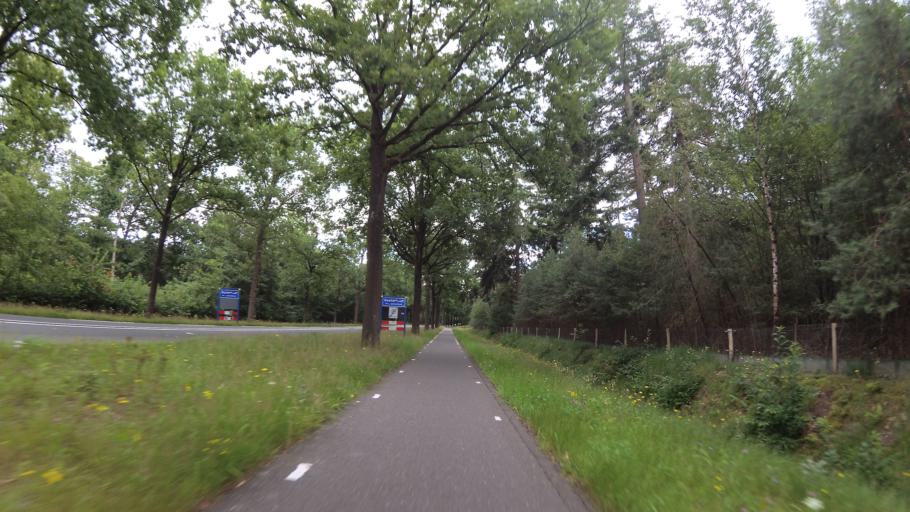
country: NL
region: North Brabant
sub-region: Gemeente Oosterhout
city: Oosterhout
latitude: 51.6172
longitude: 4.8819
